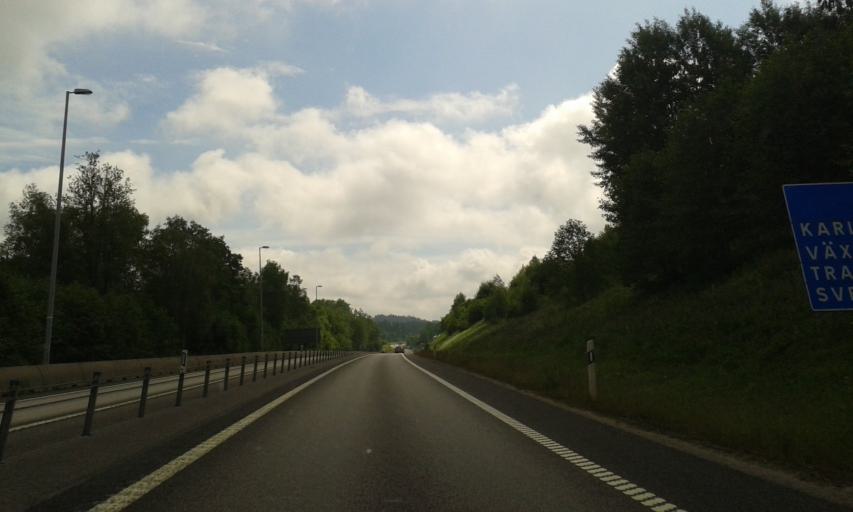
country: SE
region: Vaestra Goetaland
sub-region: Boras Kommun
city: Boras
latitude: 57.6809
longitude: 12.9487
